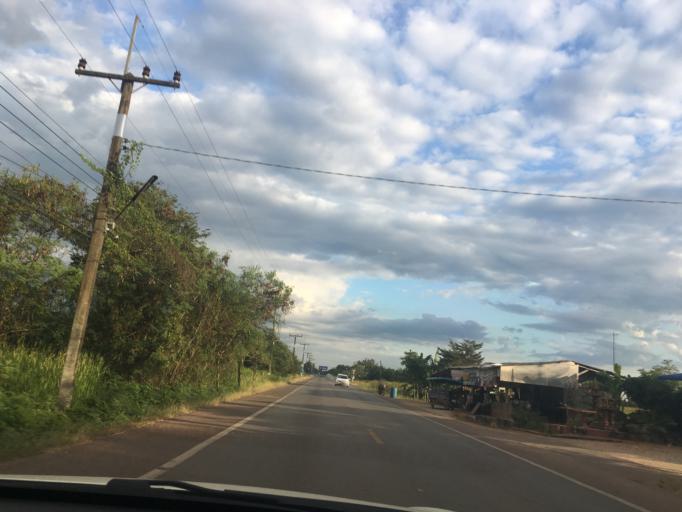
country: TH
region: Chanthaburi
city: Na Yai Am
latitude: 12.7228
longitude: 101.7596
